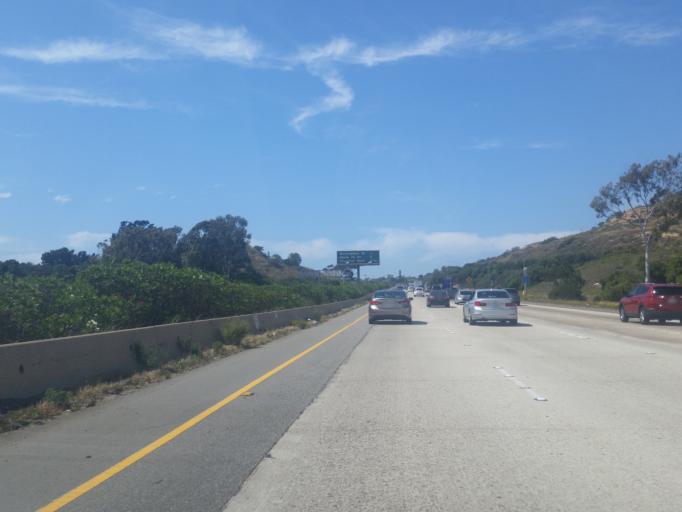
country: US
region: California
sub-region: San Diego County
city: Solana Beach
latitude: 33.0110
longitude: -117.2652
